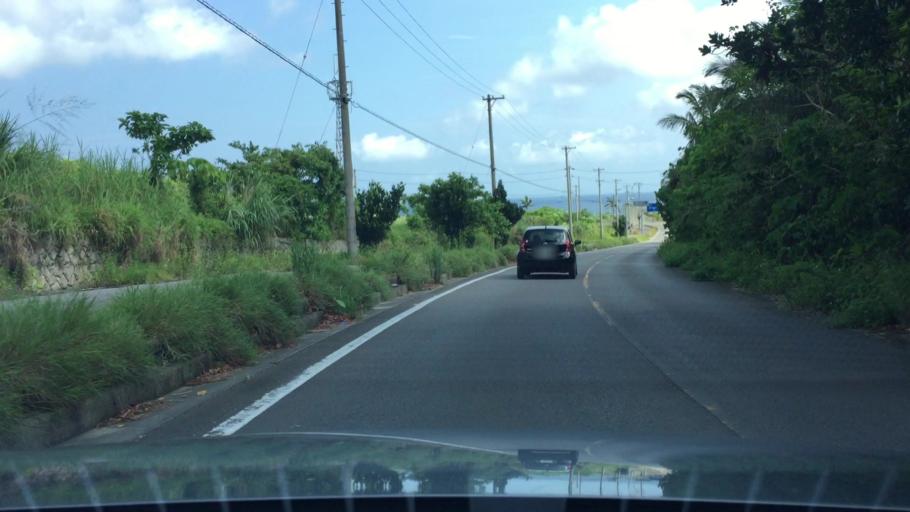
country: JP
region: Okinawa
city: Ishigaki
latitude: 24.4516
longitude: 124.2059
